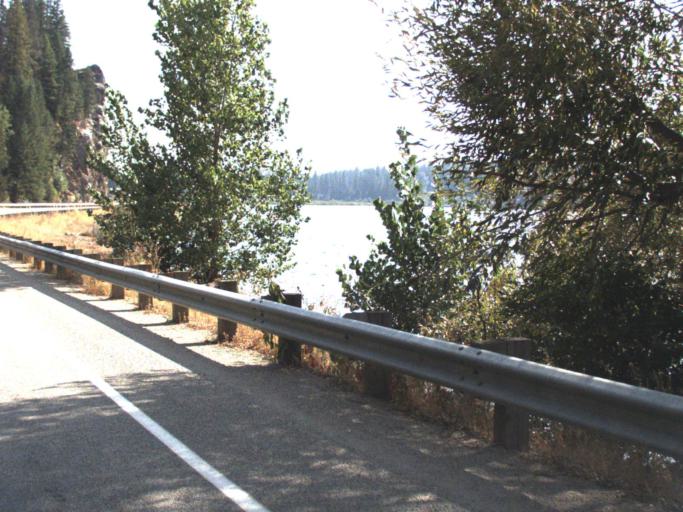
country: US
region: Washington
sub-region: Pend Oreille County
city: Newport
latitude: 48.2245
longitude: -117.2914
